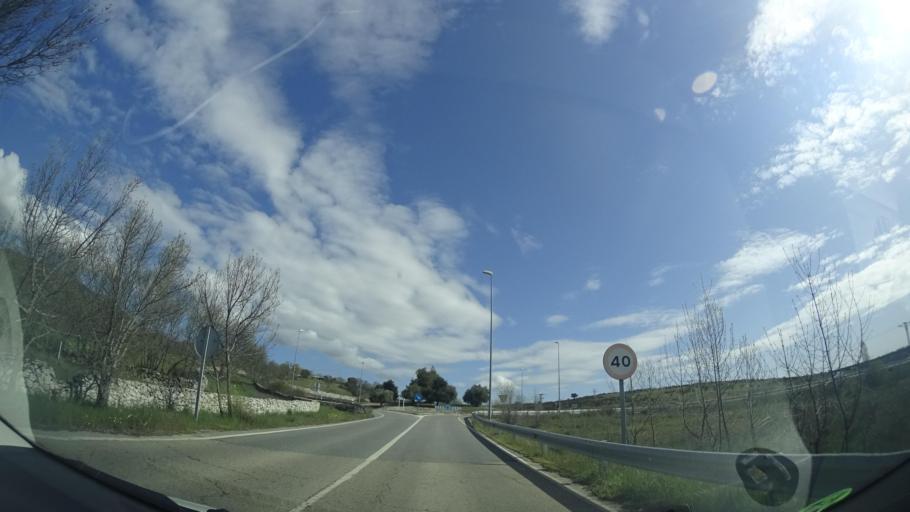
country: ES
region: Madrid
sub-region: Provincia de Madrid
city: Miraflores de la Sierra
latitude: 40.7691
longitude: -3.7805
